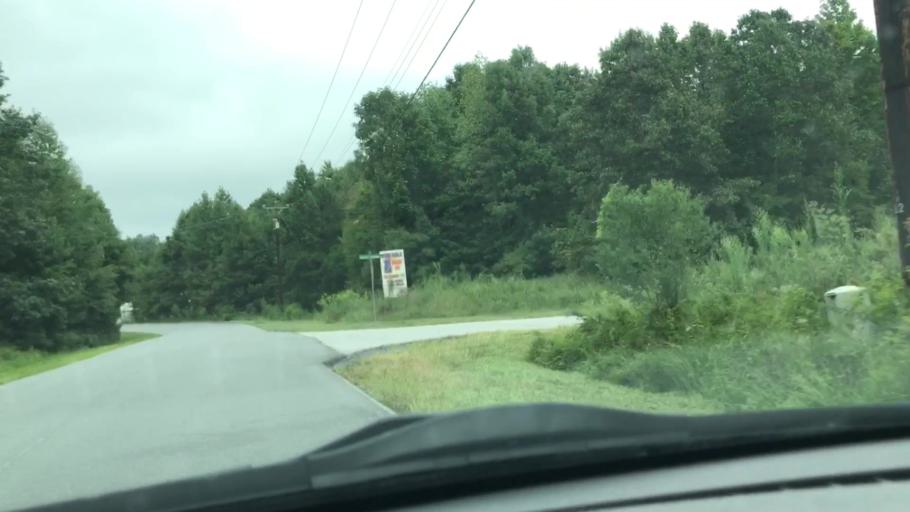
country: US
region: North Carolina
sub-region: Randolph County
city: Randleman
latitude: 35.8064
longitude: -79.8125
